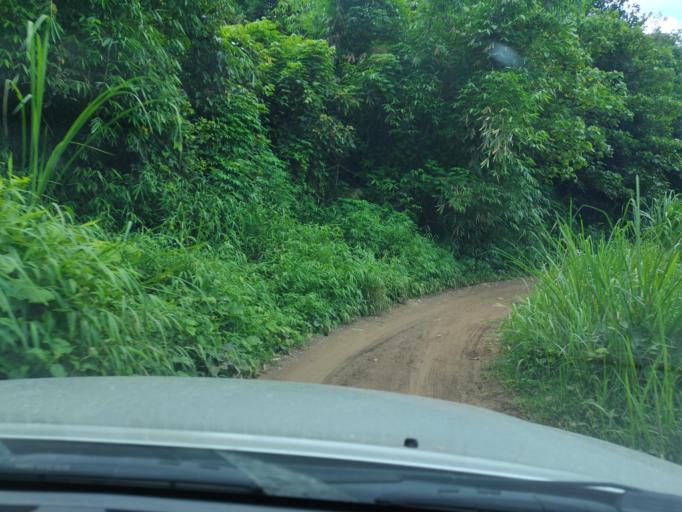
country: LA
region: Loungnamtha
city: Muang Long
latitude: 20.7570
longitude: 101.0172
